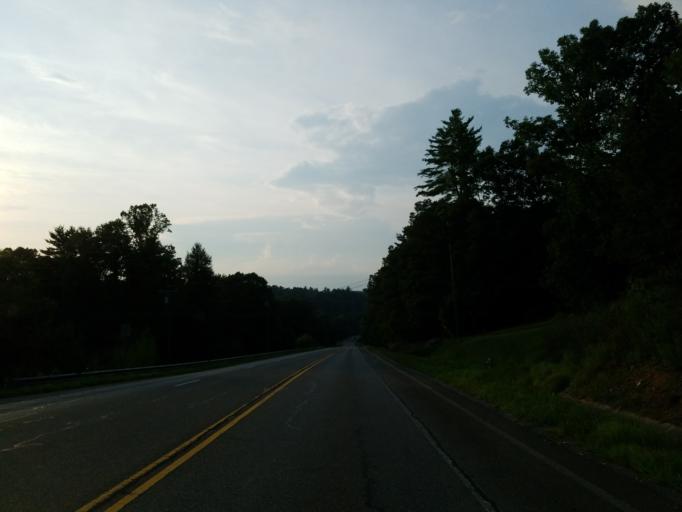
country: US
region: Georgia
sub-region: Gilmer County
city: Ellijay
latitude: 34.6689
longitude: -84.4542
